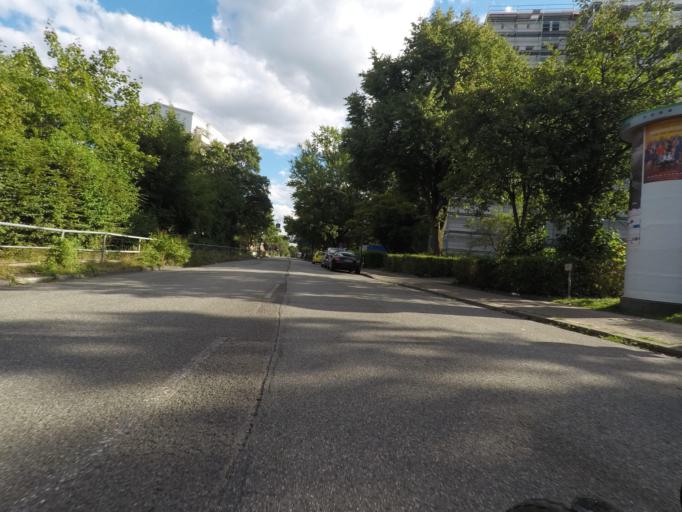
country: DE
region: Hamburg
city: Steilshoop
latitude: 53.6039
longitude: 10.0778
